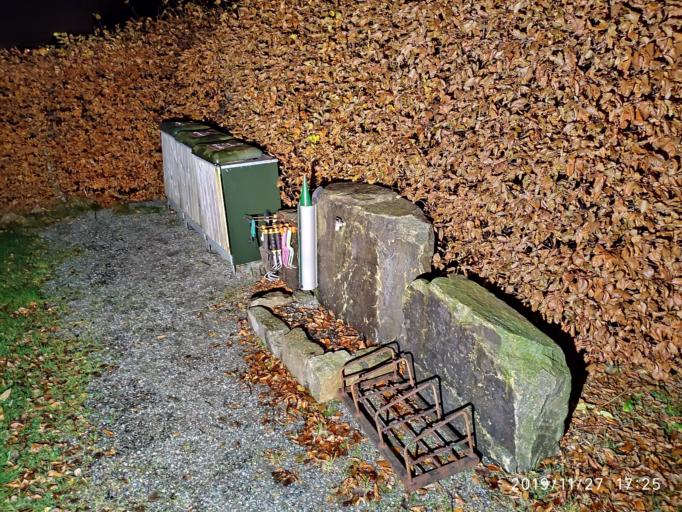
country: NO
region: Rogaland
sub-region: Lund
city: Moi
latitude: 58.4474
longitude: 6.5539
